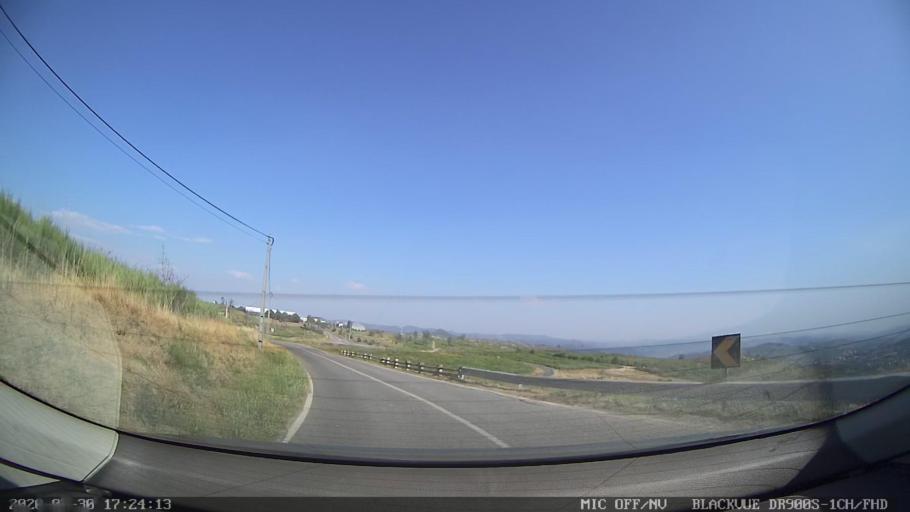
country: PT
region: Vila Real
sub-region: Murca
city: Murca
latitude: 41.3110
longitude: -7.4708
